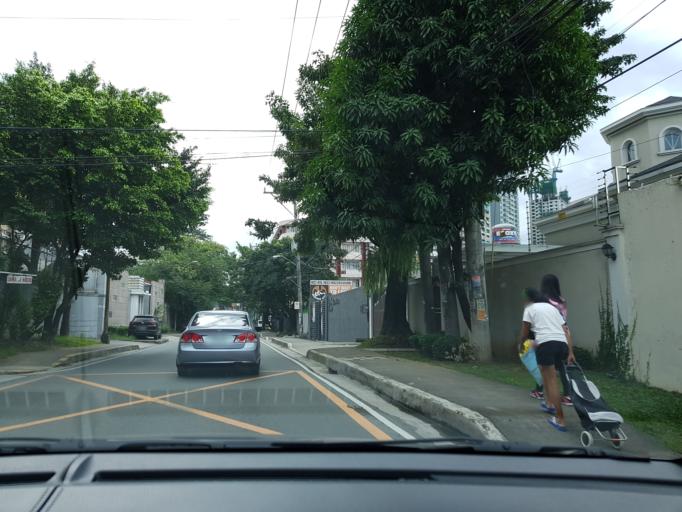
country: PH
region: Metro Manila
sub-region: San Juan
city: San Juan
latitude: 14.6182
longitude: 121.0388
